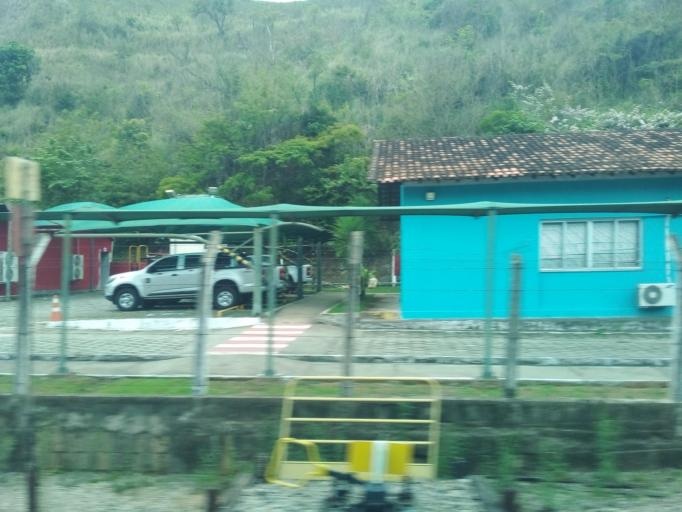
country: BR
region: Minas Gerais
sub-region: Nova Era
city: Nova Era
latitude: -19.7280
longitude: -43.0074
